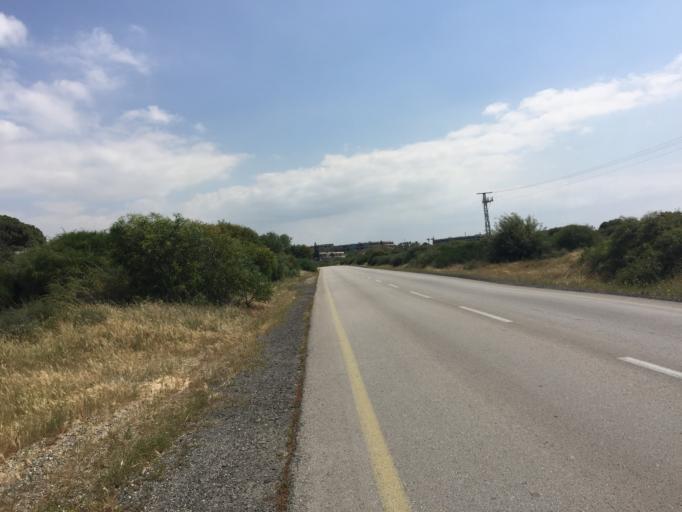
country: IL
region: Haifa
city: Qesarya
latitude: 32.4930
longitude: 34.8986
